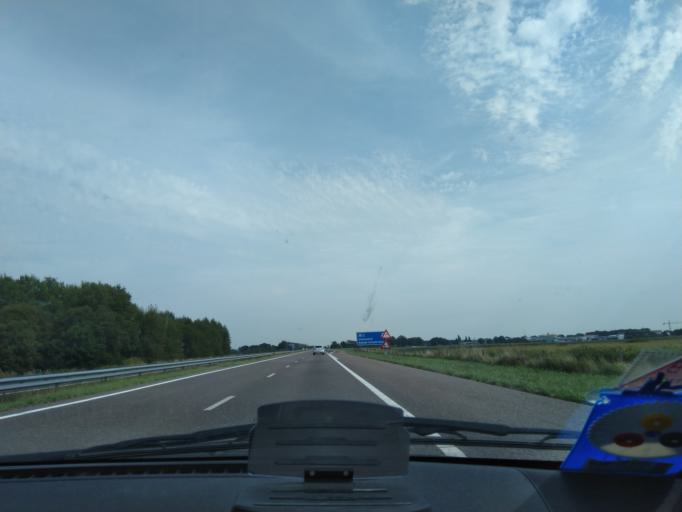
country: NL
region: Drenthe
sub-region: Gemeente Coevorden
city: Sleen
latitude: 52.7266
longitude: 6.8277
